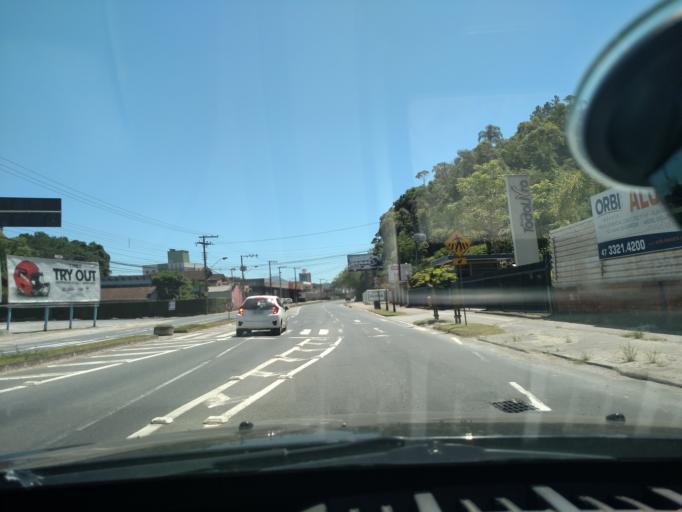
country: BR
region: Santa Catarina
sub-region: Blumenau
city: Blumenau
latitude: -26.9073
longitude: -49.0664
